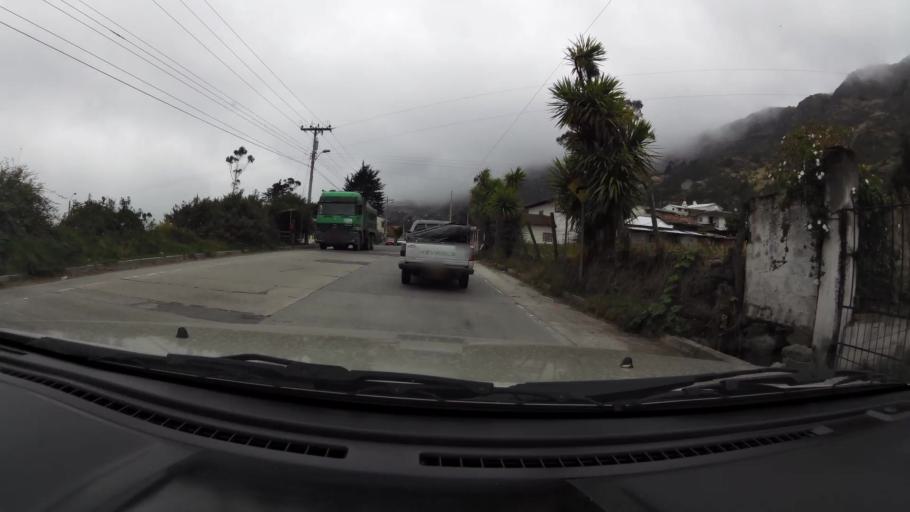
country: EC
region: Canar
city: Canar
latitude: -2.4810
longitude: -78.9825
